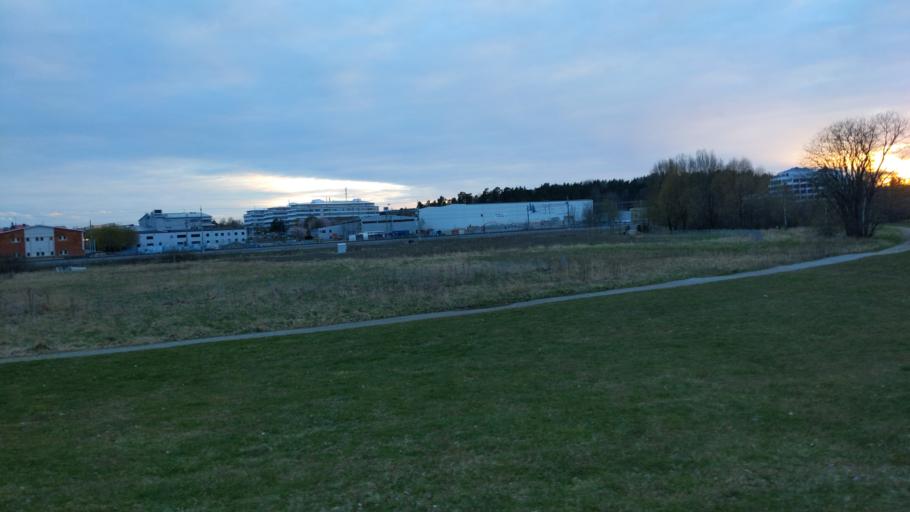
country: SE
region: Stockholm
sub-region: Stockholms Kommun
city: Kista
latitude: 59.3921
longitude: 17.8899
